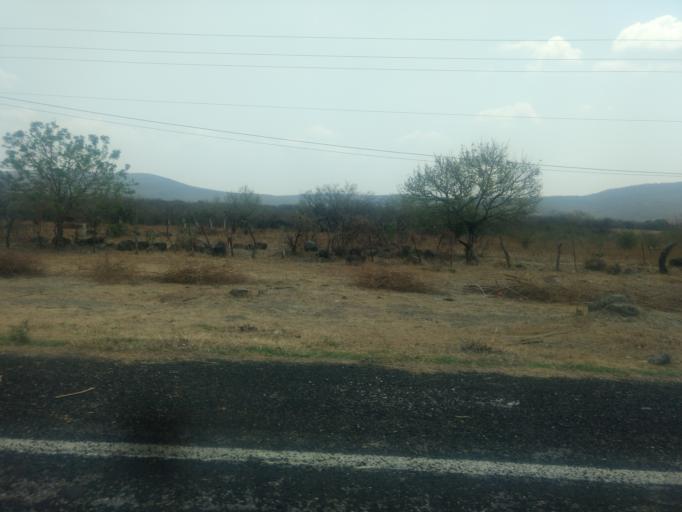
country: MX
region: Morelos
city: La Joya
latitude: 18.6740
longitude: -99.4350
